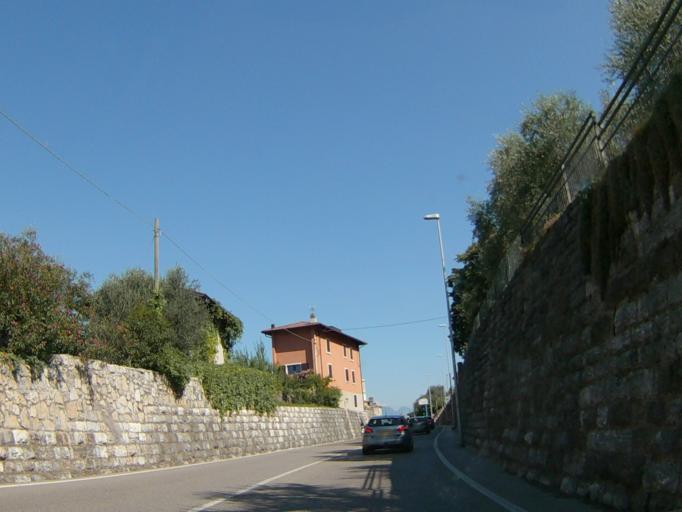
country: IT
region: Veneto
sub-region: Provincia di Verona
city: Malcesine
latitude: 45.7605
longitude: 10.8084
